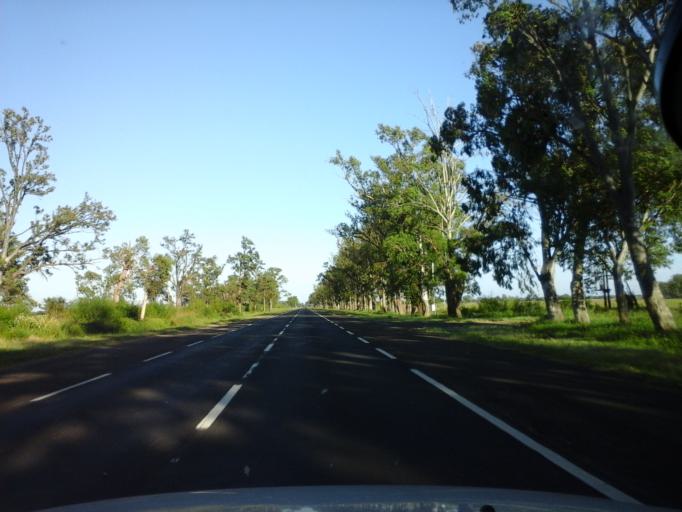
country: AR
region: Corrientes
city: Ita Ibate
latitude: -27.4543
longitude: -57.3245
